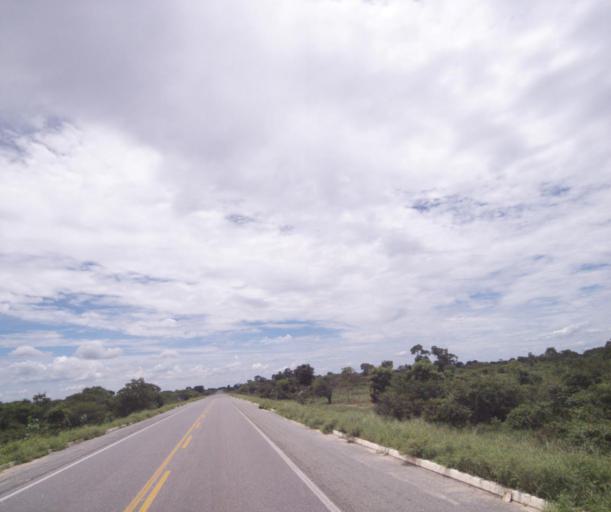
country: BR
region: Bahia
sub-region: Carinhanha
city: Carinhanha
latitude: -14.3026
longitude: -43.7853
